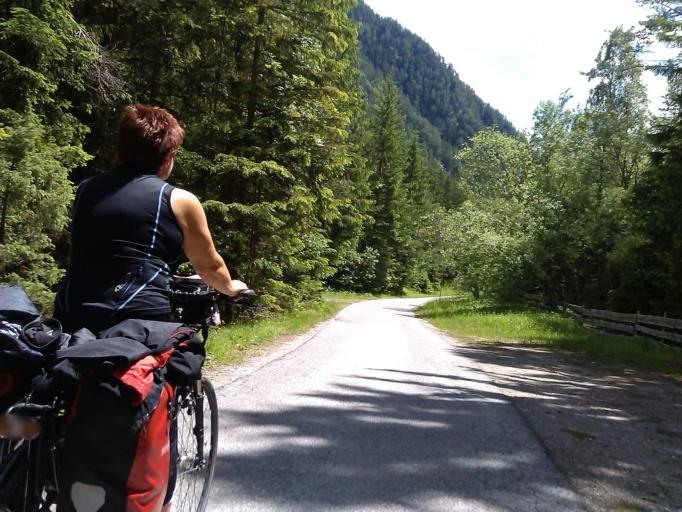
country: AT
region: Tyrol
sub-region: Politischer Bezirk Imst
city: Nassereith
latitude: 47.3390
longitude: 10.8172
